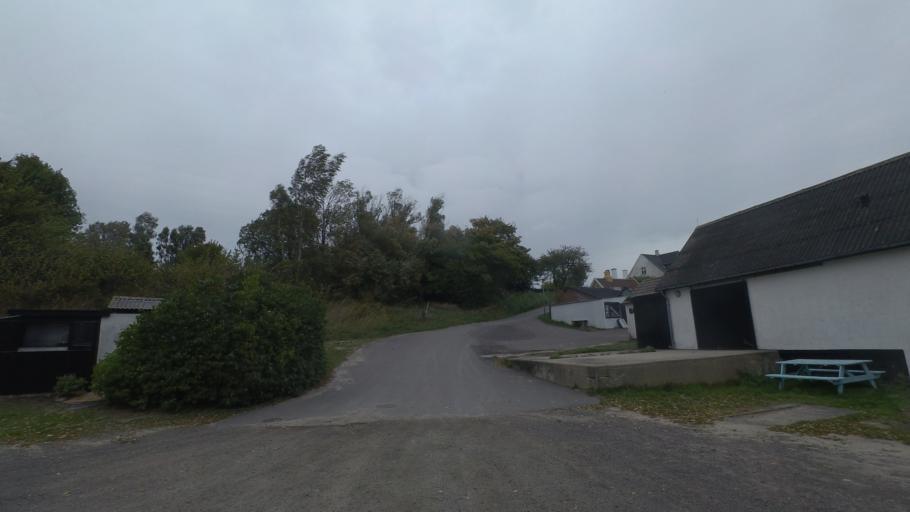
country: DK
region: Capital Region
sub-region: Bornholm Kommune
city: Akirkeby
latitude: 55.0004
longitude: 14.9891
